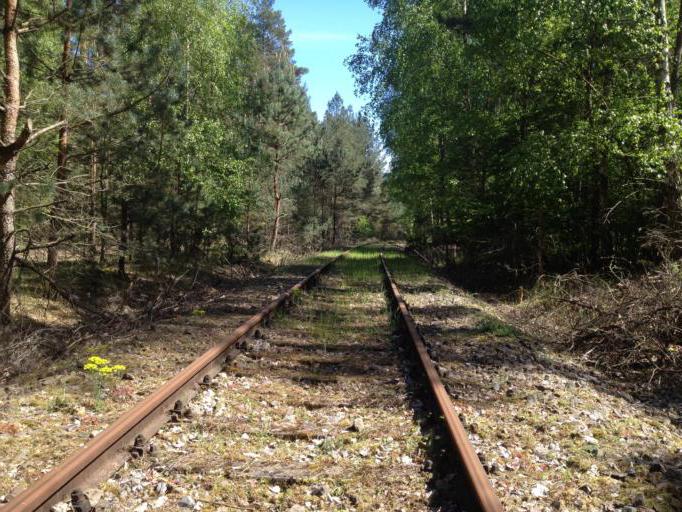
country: DE
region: Brandenburg
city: Templin
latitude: 53.1506
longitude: 13.4021
